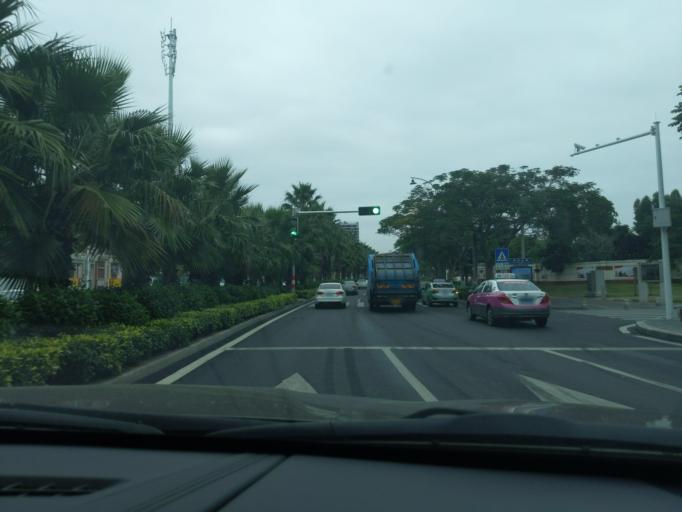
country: CN
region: Fujian
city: Liuwudian
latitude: 24.4961
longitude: 118.1702
